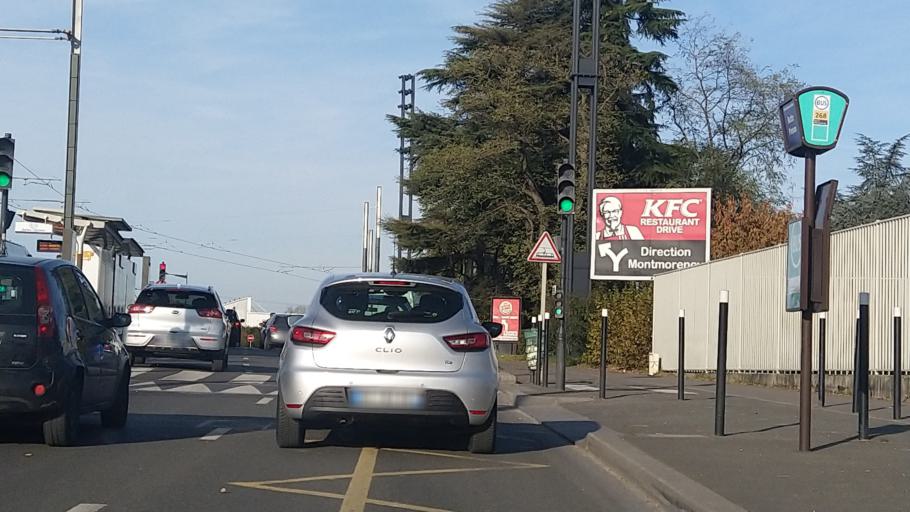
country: FR
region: Ile-de-France
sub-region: Departement de Seine-Saint-Denis
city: Pierrefitte-sur-Seine
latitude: 48.9735
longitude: 2.3667
